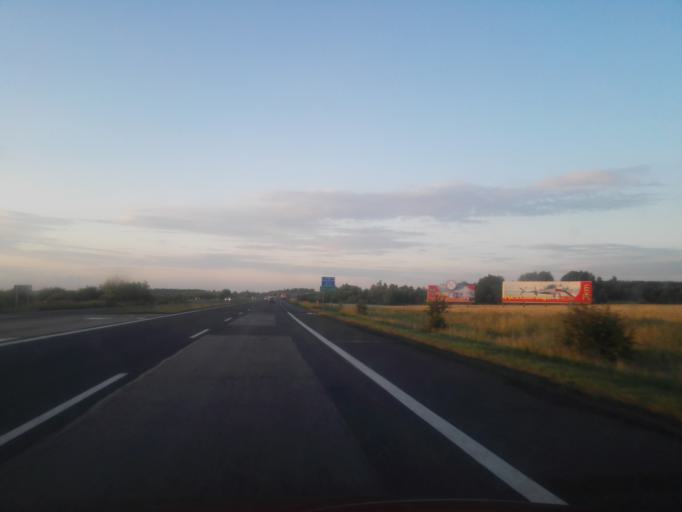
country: PL
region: Silesian Voivodeship
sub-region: Powiat czestochowski
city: Koscielec
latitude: 50.8817
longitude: 19.1668
